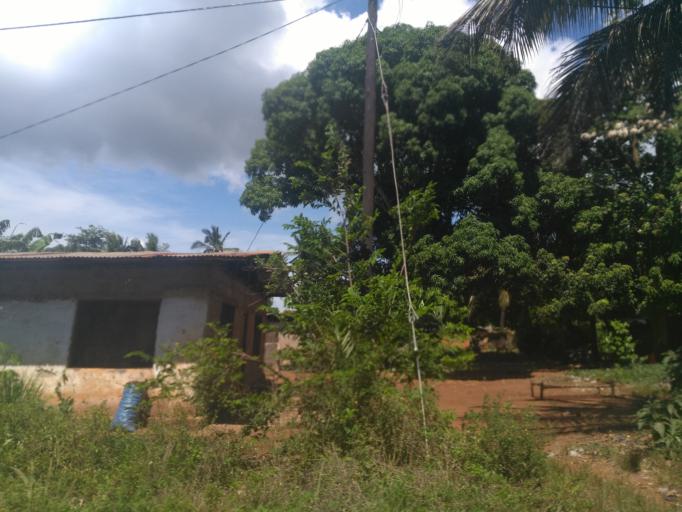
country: TZ
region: Zanzibar North
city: Gamba
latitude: -5.9380
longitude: 39.3401
